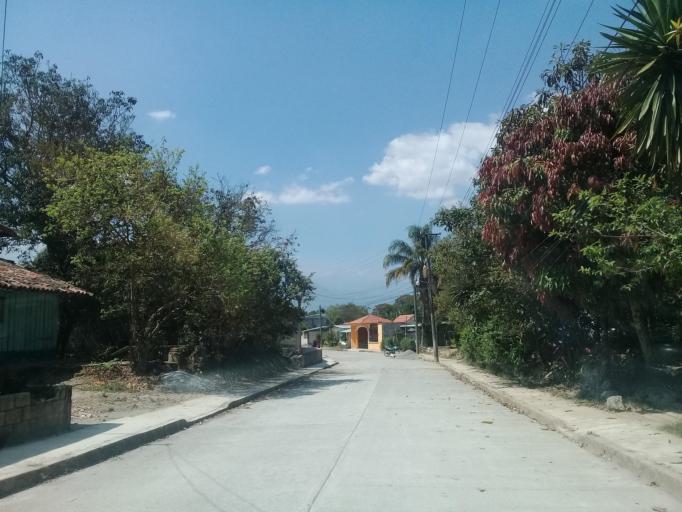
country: MX
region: Veracruz
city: Jalapilla
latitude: 18.8109
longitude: -97.0665
